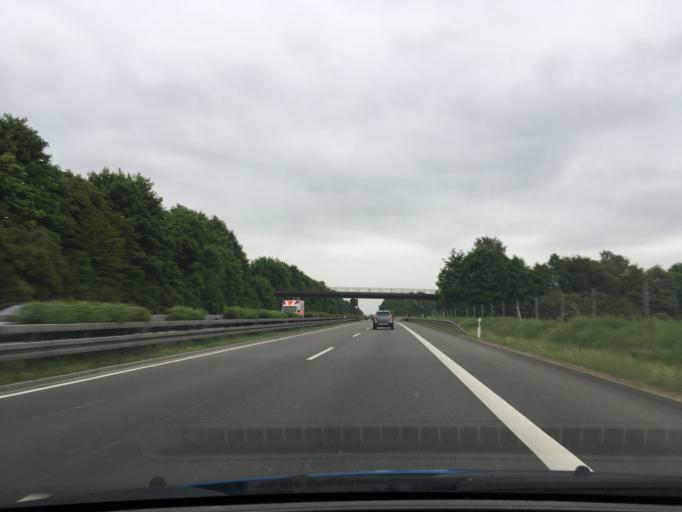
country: DE
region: Lower Saxony
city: Stelle
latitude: 53.3772
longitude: 10.0889
